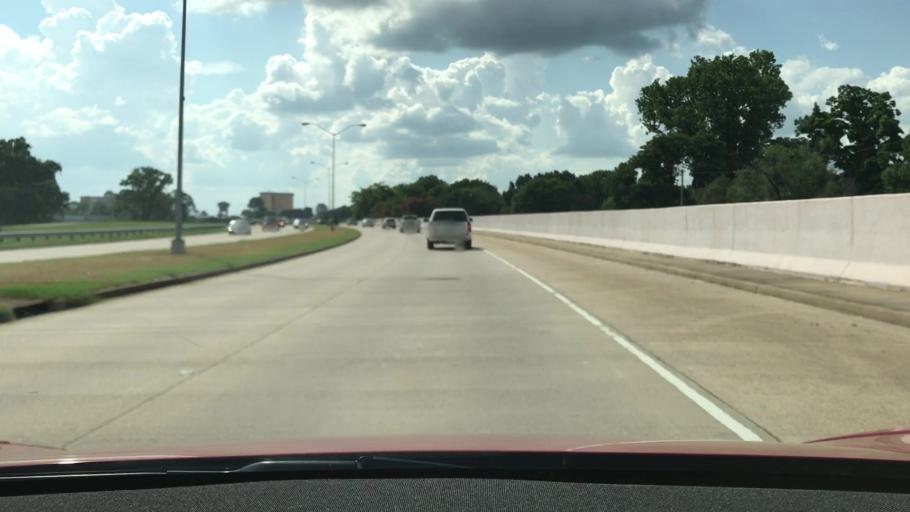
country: US
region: Louisiana
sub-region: Bossier Parish
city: Bossier City
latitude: 32.5091
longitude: -93.7162
